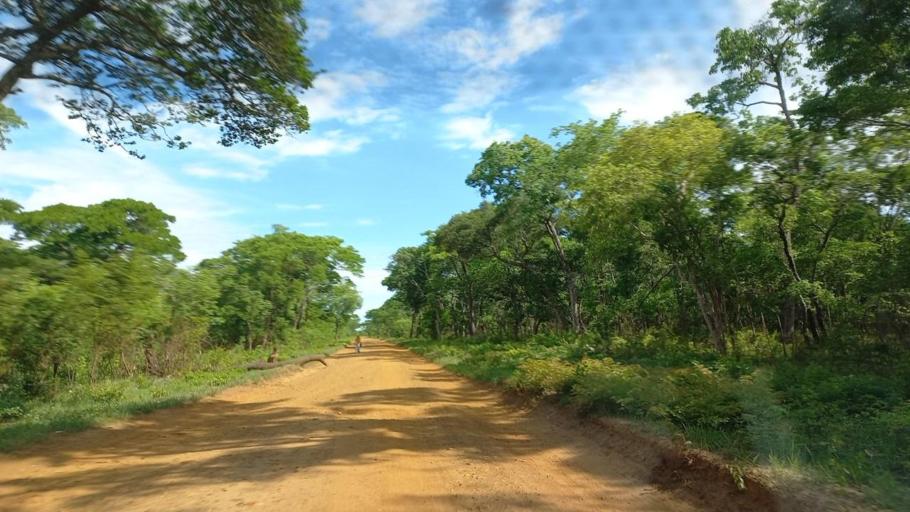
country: ZM
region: North-Western
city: Kabompo
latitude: -13.0801
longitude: 24.2195
